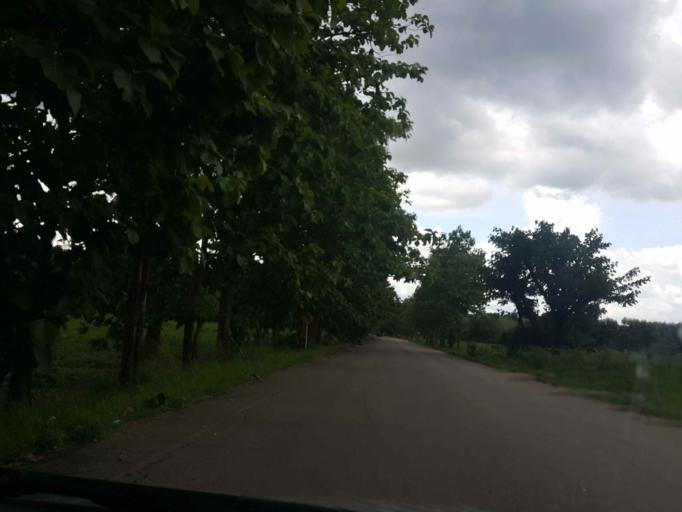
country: TH
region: Phayao
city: Dok Kham Tai
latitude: 18.9842
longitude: 100.0682
